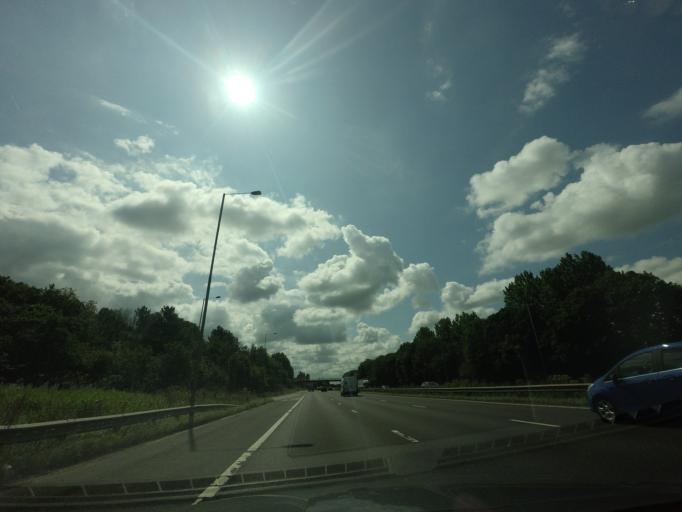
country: GB
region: England
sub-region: Lancashire
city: Clayton-le-Woods
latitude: 53.6937
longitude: -2.6774
